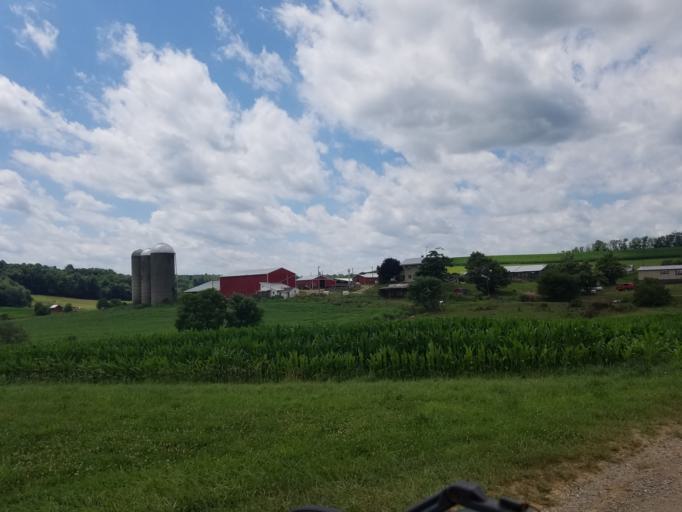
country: US
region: Ohio
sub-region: Knox County
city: Danville
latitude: 40.5465
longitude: -82.3452
